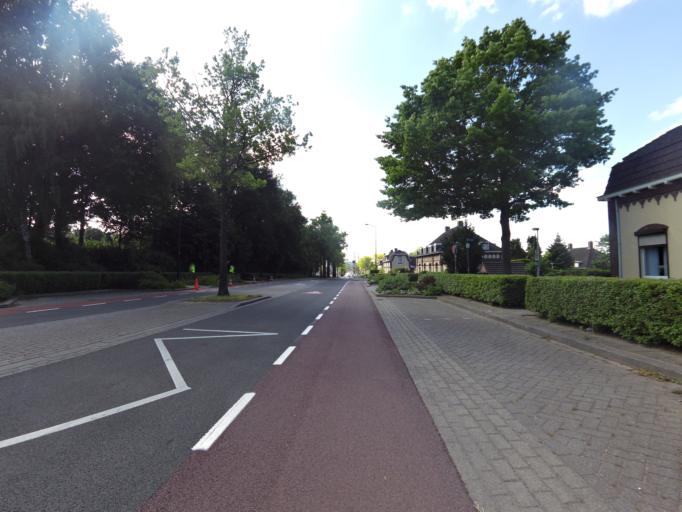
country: NL
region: Limburg
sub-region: Gemeente Heerlen
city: Heerlen
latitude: 50.9076
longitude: 5.9653
